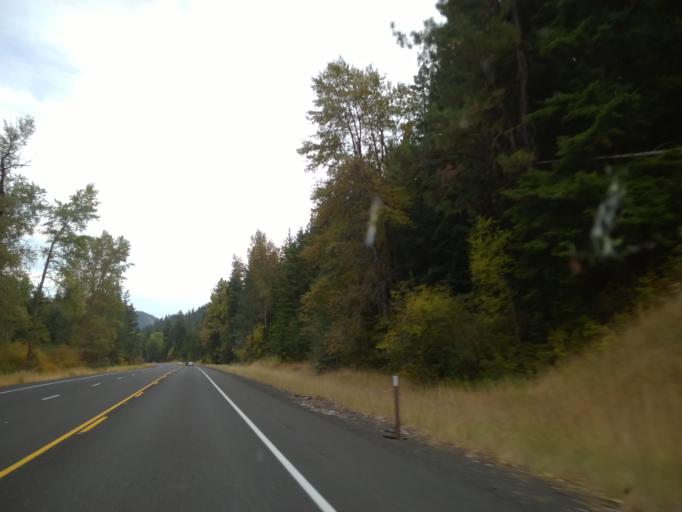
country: US
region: Washington
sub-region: Kittitas County
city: Cle Elum
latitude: 47.2677
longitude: -120.6978
